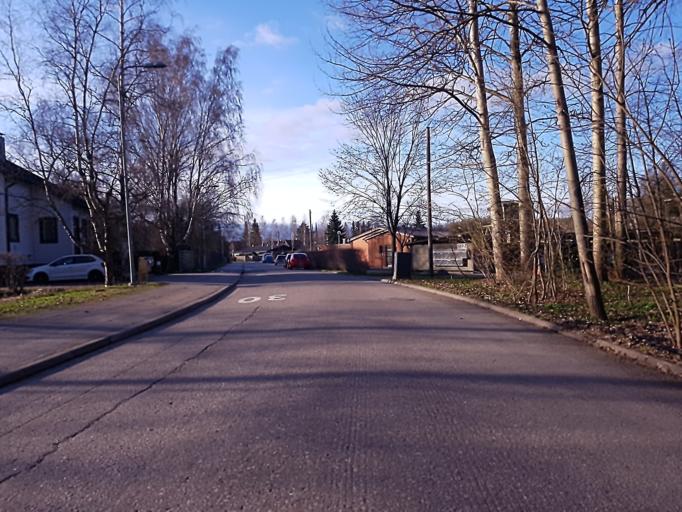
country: FI
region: Uusimaa
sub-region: Helsinki
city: Helsinki
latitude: 60.2532
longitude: 24.9467
